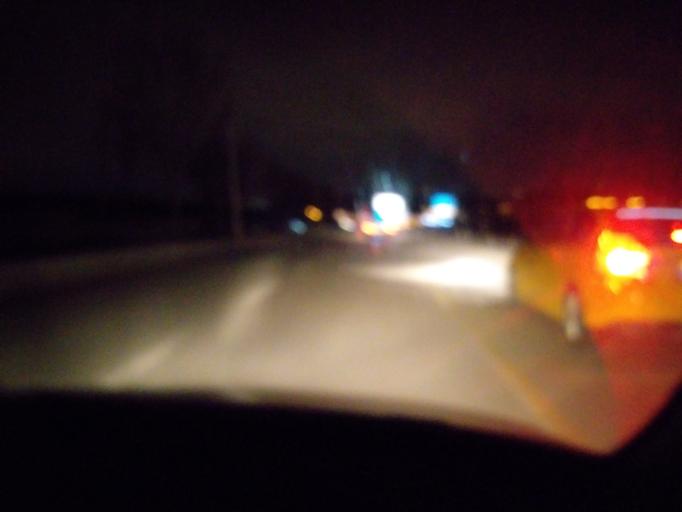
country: TR
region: Ankara
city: Batikent
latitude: 39.9019
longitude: 32.7332
